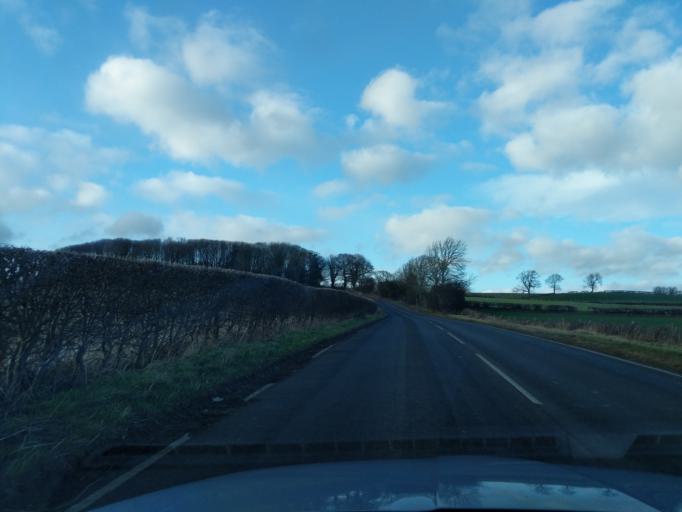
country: GB
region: England
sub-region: North Yorkshire
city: Catterick Garrison
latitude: 54.3389
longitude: -1.6872
